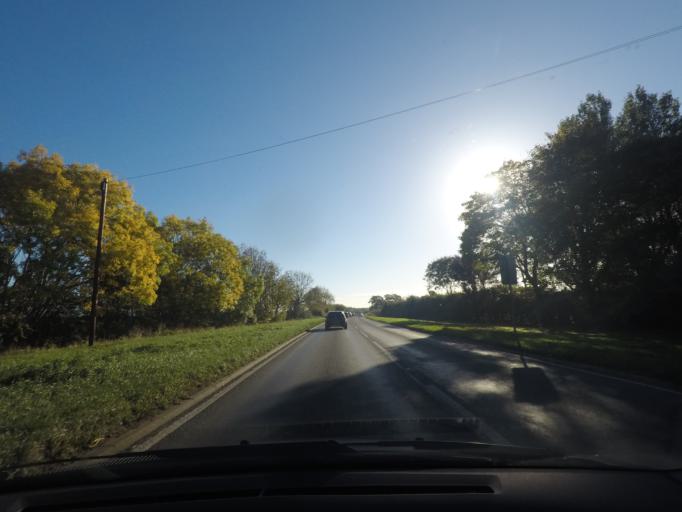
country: GB
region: England
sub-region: East Riding of Yorkshire
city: Wilberfoss
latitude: 53.9459
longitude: -0.8812
